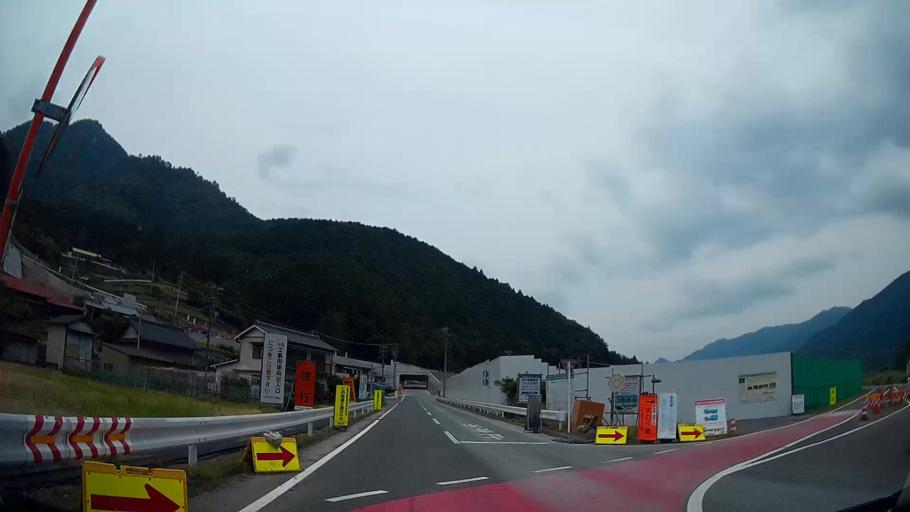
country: JP
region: Shizuoka
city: Hamakita
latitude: 35.0730
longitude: 137.7894
